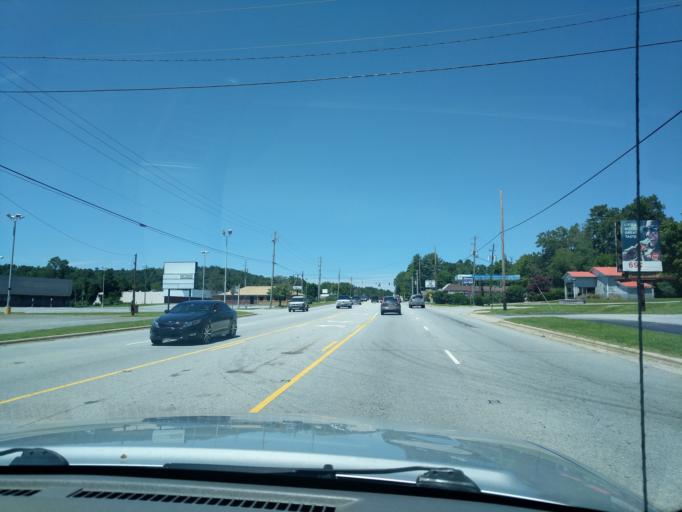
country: US
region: North Carolina
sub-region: Henderson County
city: Fletcher
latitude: 35.4466
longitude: -82.5077
